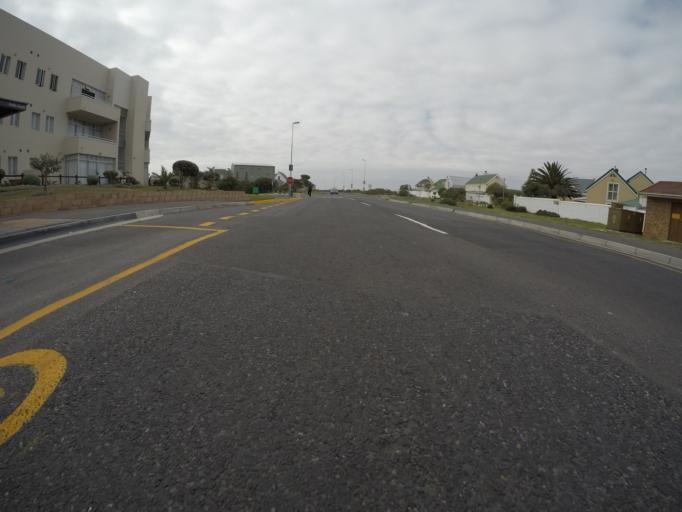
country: ZA
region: Western Cape
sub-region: City of Cape Town
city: Atlantis
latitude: -33.7114
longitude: 18.4462
